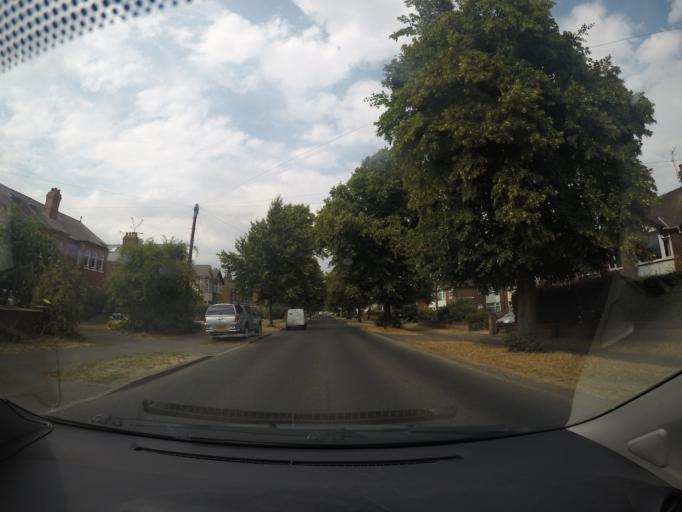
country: GB
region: England
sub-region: City of York
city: Nether Poppleton
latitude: 53.9592
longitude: -1.1352
